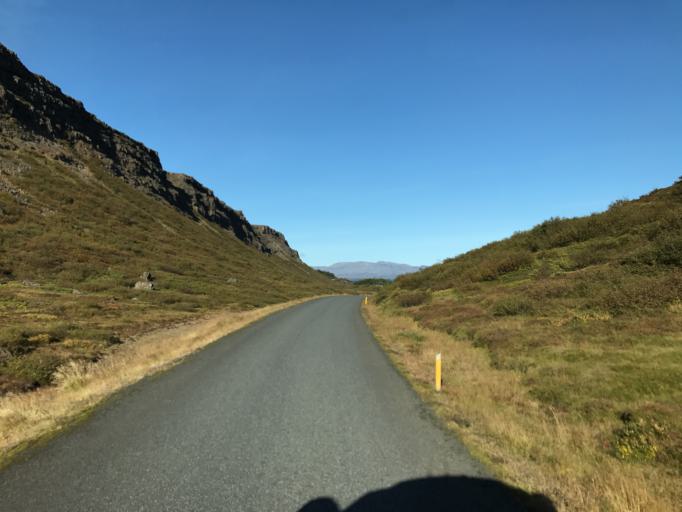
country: IS
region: South
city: Hveragerdi
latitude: 64.1656
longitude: -21.2416
